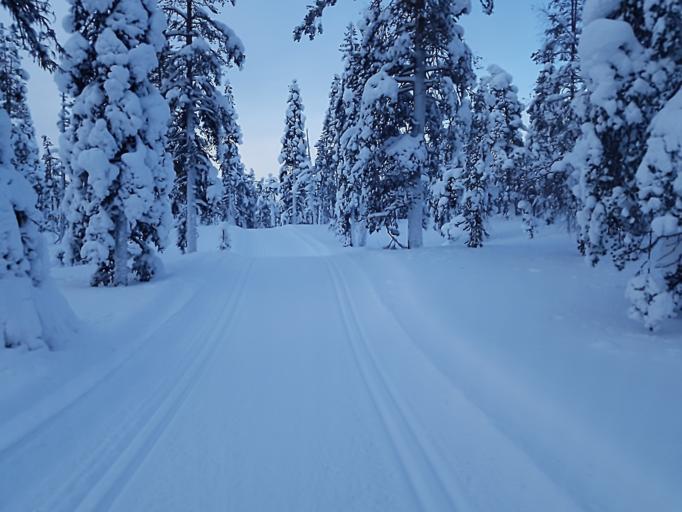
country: FI
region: Lapland
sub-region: Tunturi-Lappi
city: Kolari
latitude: 67.6550
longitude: 24.2491
